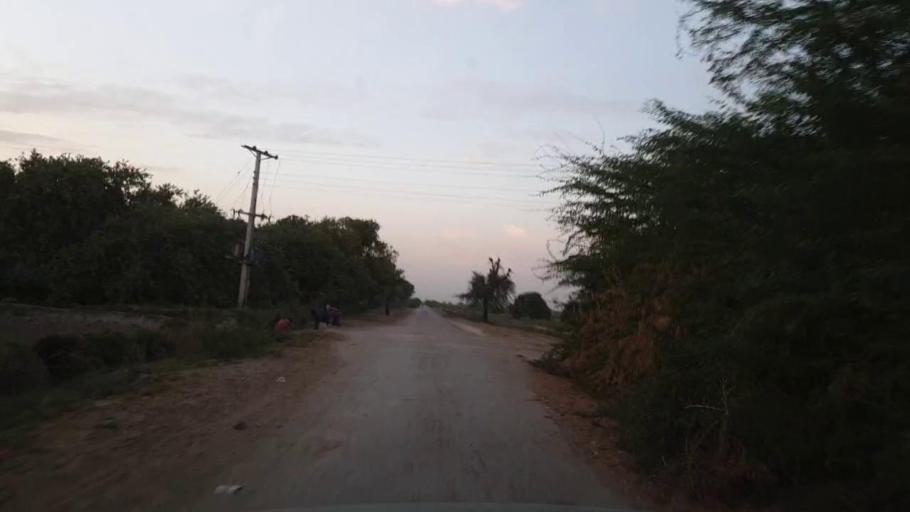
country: PK
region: Sindh
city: Kunri
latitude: 25.1466
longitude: 69.5573
